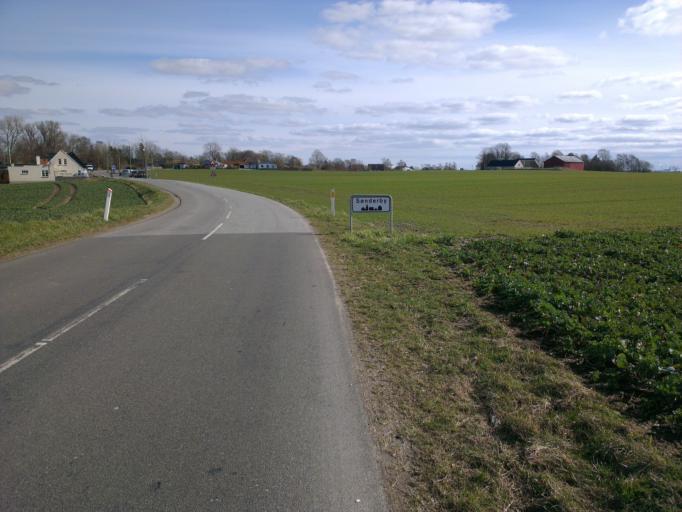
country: DK
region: Capital Region
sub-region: Frederikssund Kommune
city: Skibby
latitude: 55.7381
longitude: 12.0234
